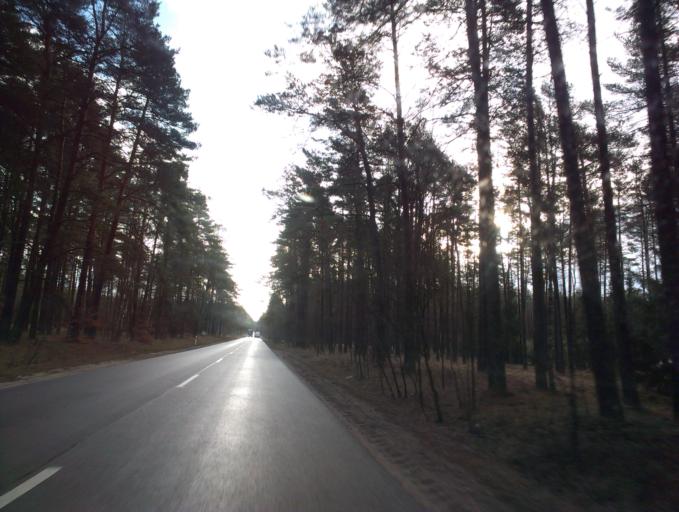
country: PL
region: Pomeranian Voivodeship
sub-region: Powiat czluchowski
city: Czarne
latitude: 53.6980
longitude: 16.8906
